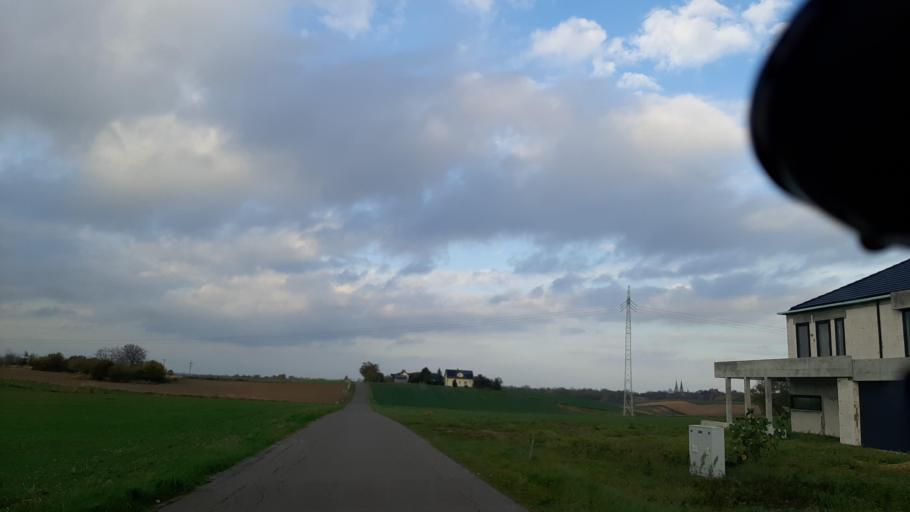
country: PL
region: Lublin Voivodeship
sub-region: Powiat lubelski
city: Garbow
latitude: 51.3375
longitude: 22.3243
